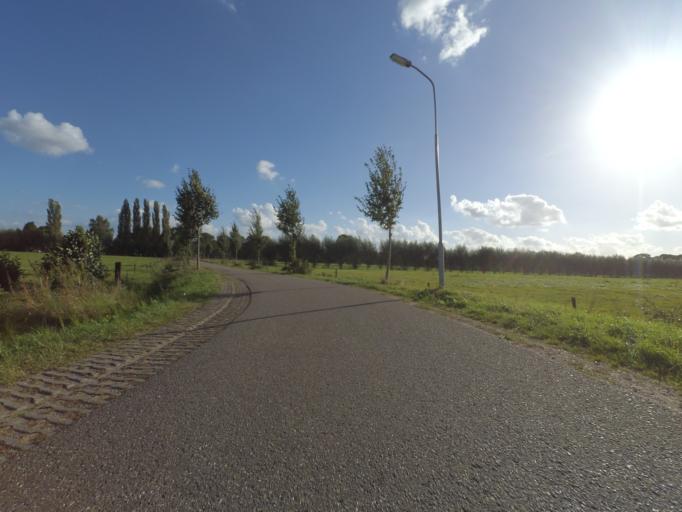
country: NL
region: Gelderland
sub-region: Gemeente Barneveld
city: Terschuur
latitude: 52.1163
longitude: 5.5104
